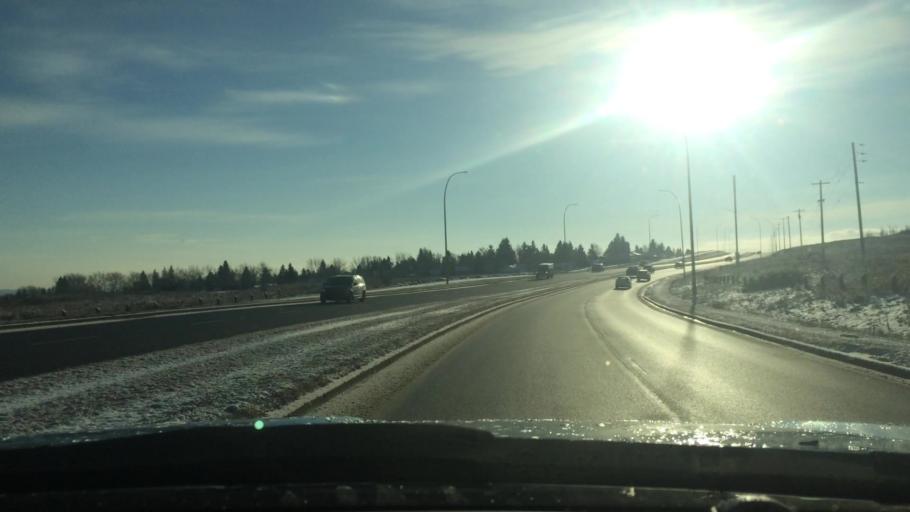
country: CA
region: Alberta
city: Calgary
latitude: 51.1248
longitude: -114.0965
